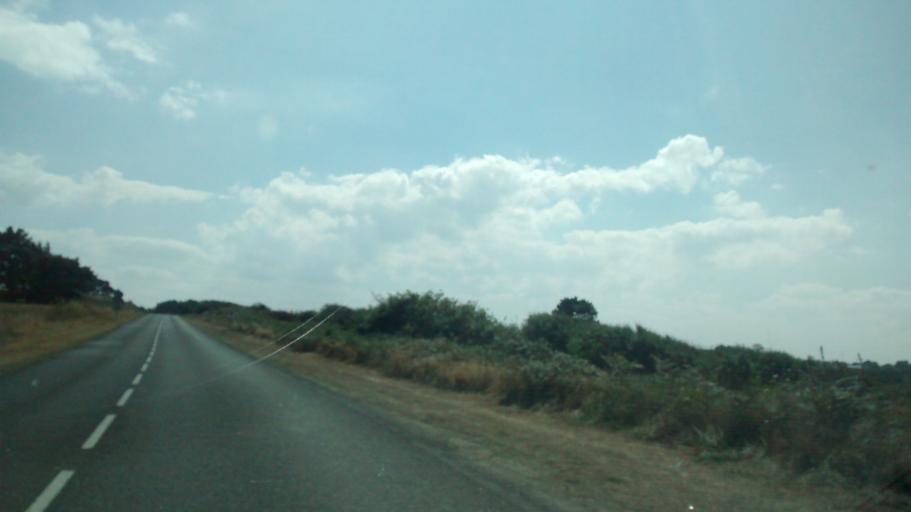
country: FR
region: Brittany
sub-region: Departement d'Ille-et-Vilaine
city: Cancale
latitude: 48.7000
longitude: -1.8603
